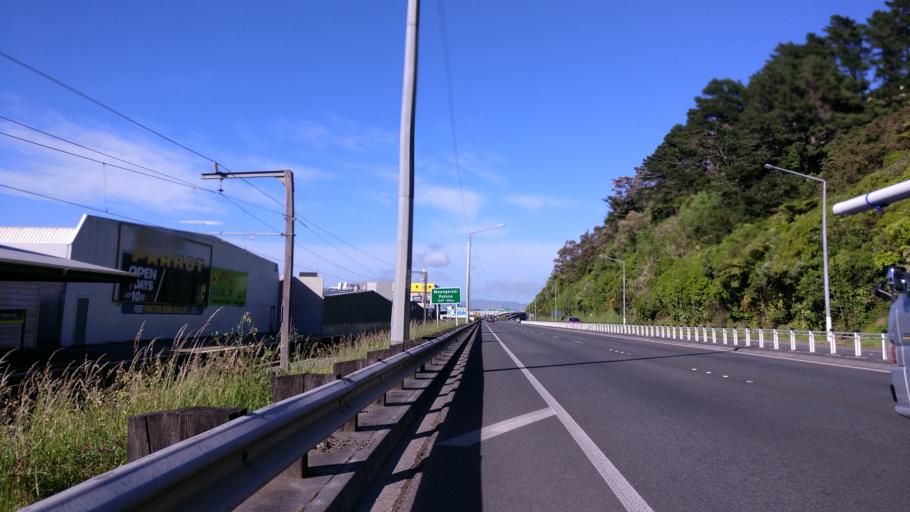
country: NZ
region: Wellington
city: Petone
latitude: -41.2117
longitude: 174.8898
